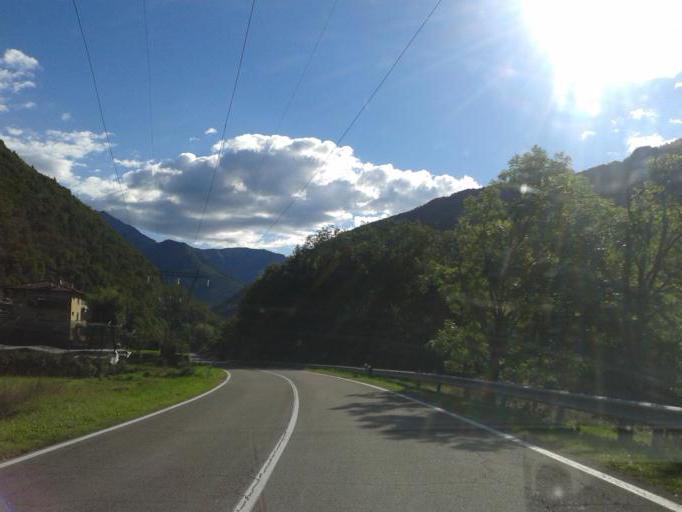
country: IT
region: Trentino-Alto Adige
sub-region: Provincia di Trento
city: Pieve di Ledro
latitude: 45.8923
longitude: 10.6872
